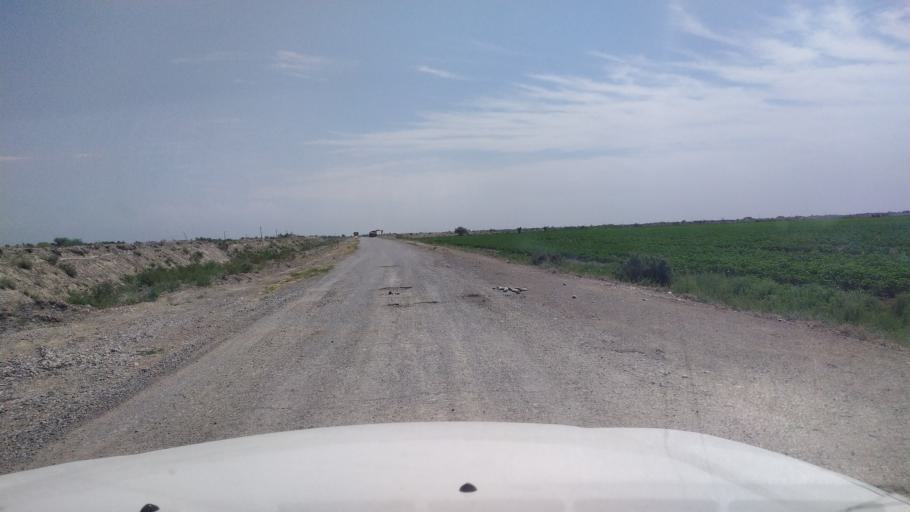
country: UZ
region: Namangan
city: Toshbuloq
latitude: 40.7895
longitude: 71.5636
